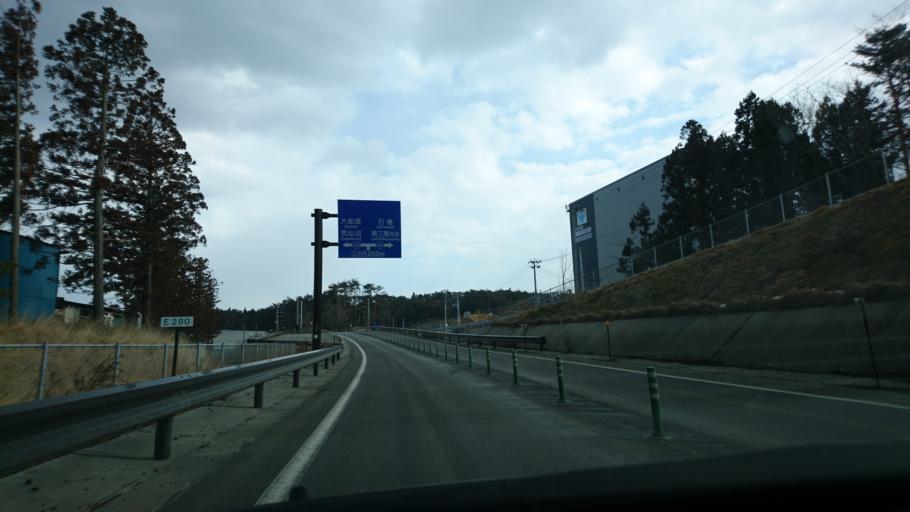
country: JP
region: Miyagi
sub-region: Oshika Gun
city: Onagawa Cho
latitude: 38.6922
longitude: 141.4638
